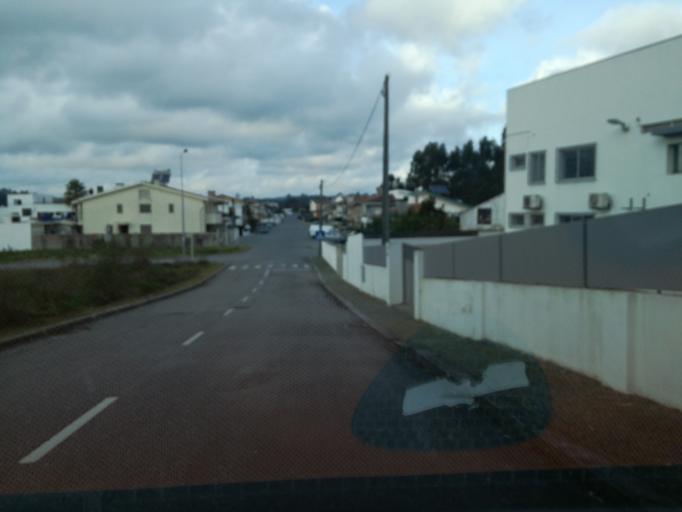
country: PT
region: Porto
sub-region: Maia
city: Nogueira
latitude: 41.2532
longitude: -8.5971
